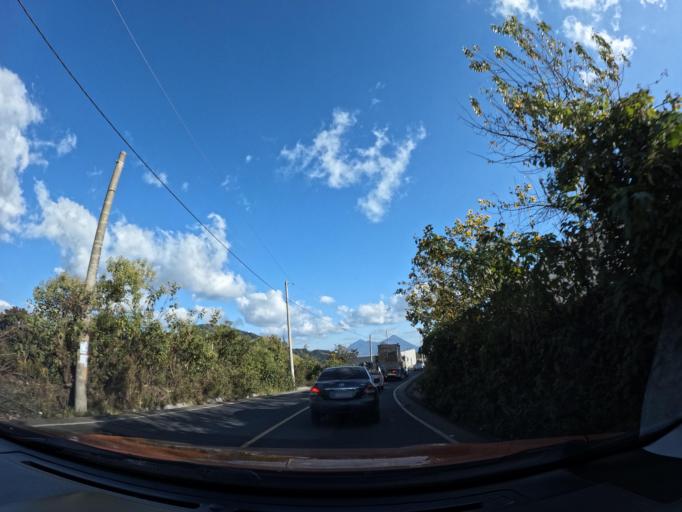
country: GT
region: Sacatepequez
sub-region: Municipio de Santa Maria de Jesus
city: Santa Maria de Jesus
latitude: 14.4876
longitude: -90.7065
